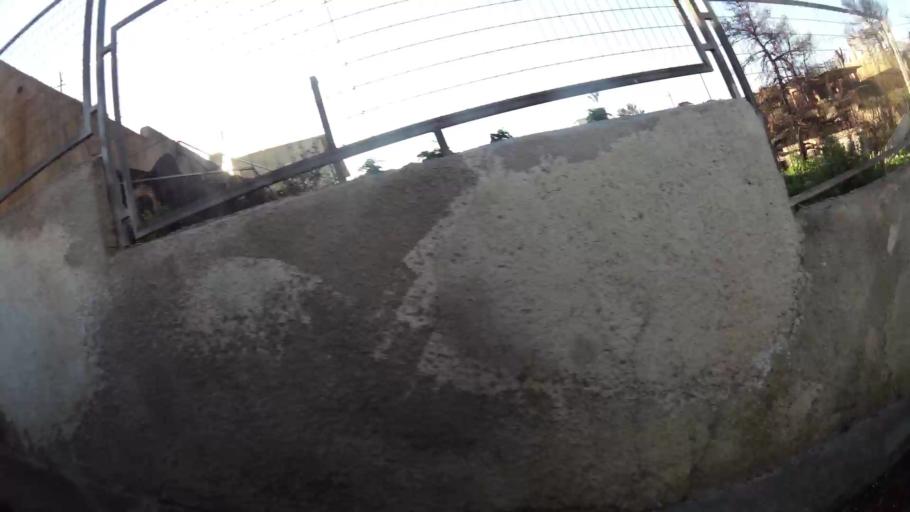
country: GR
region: Attica
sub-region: Nomarchia Anatolikis Attikis
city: Rafina
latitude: 38.0311
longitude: 23.9987
